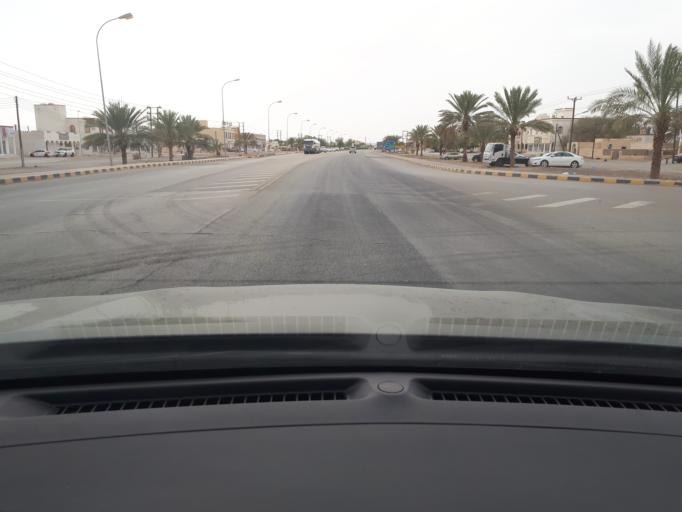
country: OM
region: Ash Sharqiyah
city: Badiyah
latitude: 22.4511
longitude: 58.8151
